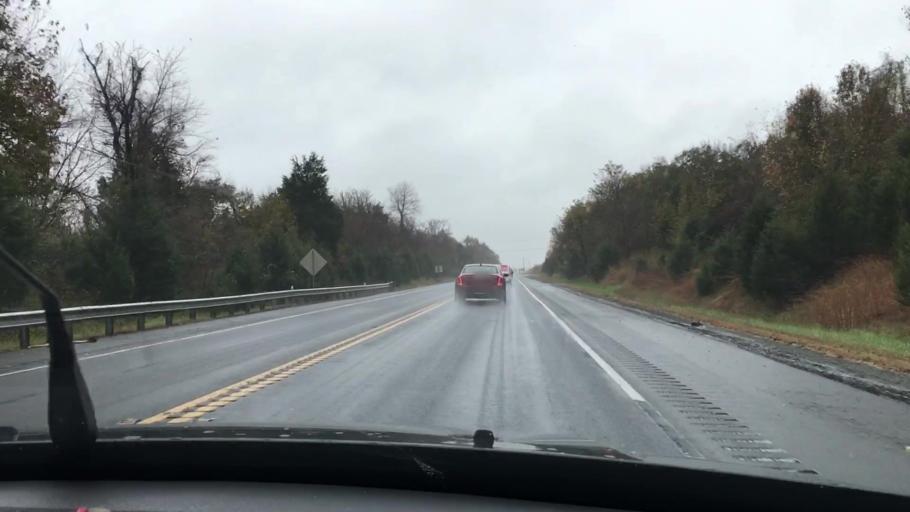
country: US
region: Virginia
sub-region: Loudoun County
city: Leesburg
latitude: 39.1336
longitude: -77.5460
